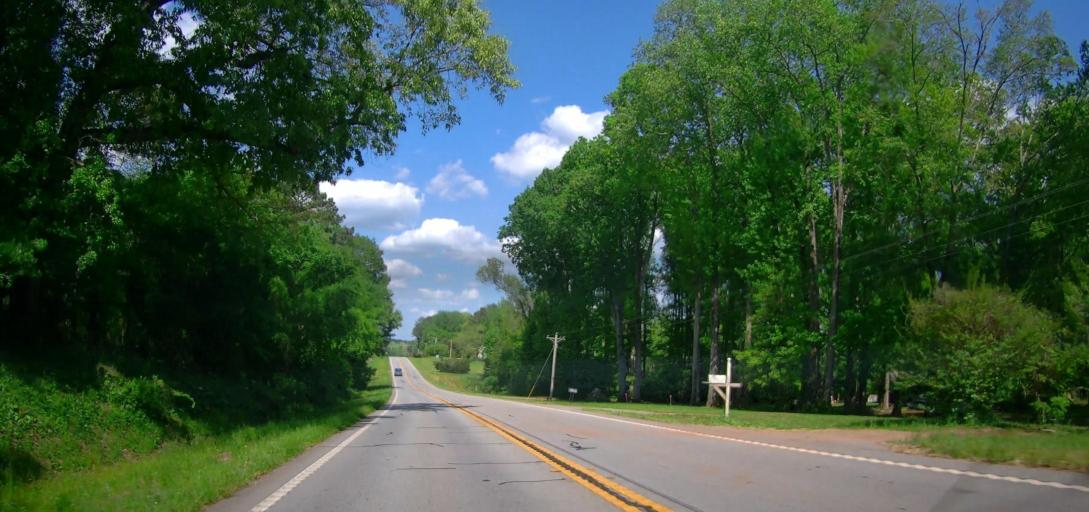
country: US
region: Georgia
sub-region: Greene County
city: Greensboro
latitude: 33.5727
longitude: -83.2220
